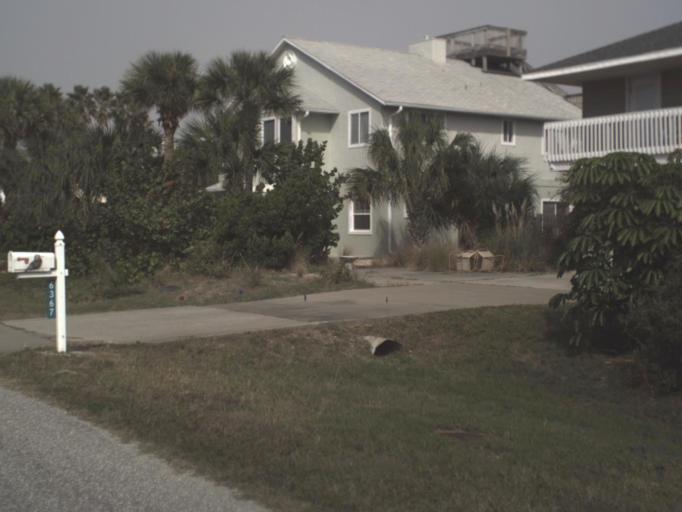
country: US
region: Florida
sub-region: Volusia County
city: Edgewater
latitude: 28.9570
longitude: -80.8445
